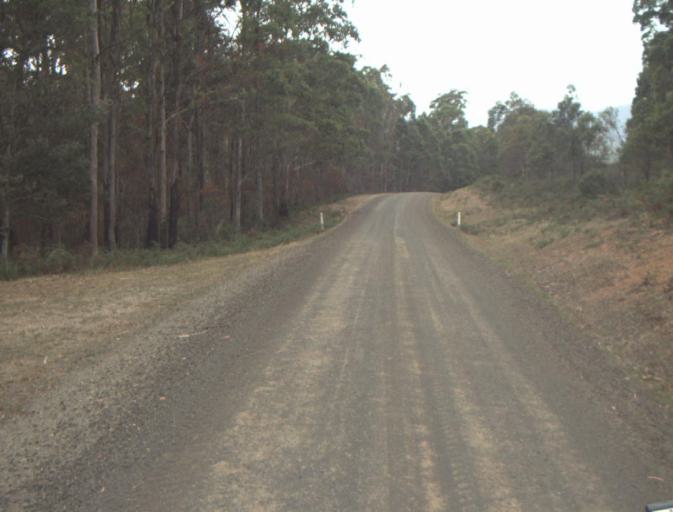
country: AU
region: Tasmania
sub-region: Dorset
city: Scottsdale
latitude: -41.4463
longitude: 147.5210
